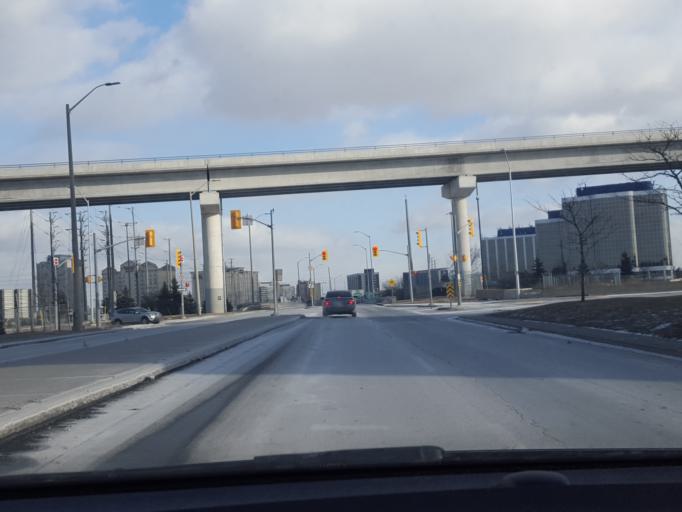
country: CA
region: Ontario
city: Etobicoke
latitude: 43.6901
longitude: -79.6147
